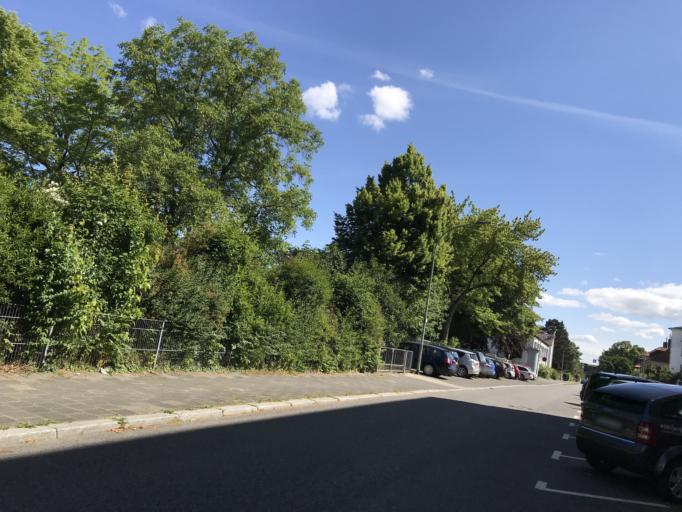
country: DE
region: Hesse
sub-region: Regierungsbezirk Darmstadt
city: Friedberg
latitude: 50.3292
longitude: 8.7540
